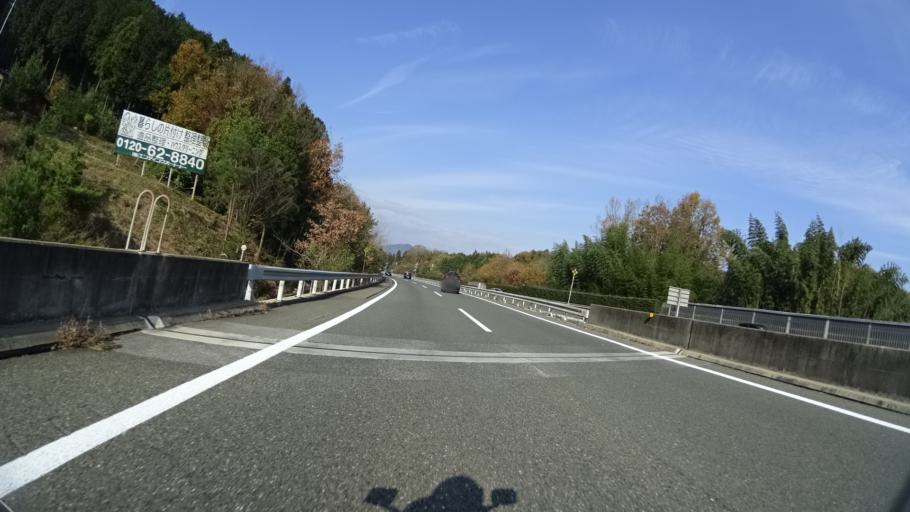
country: JP
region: Kyoto
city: Kameoka
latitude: 35.0010
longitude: 135.5714
